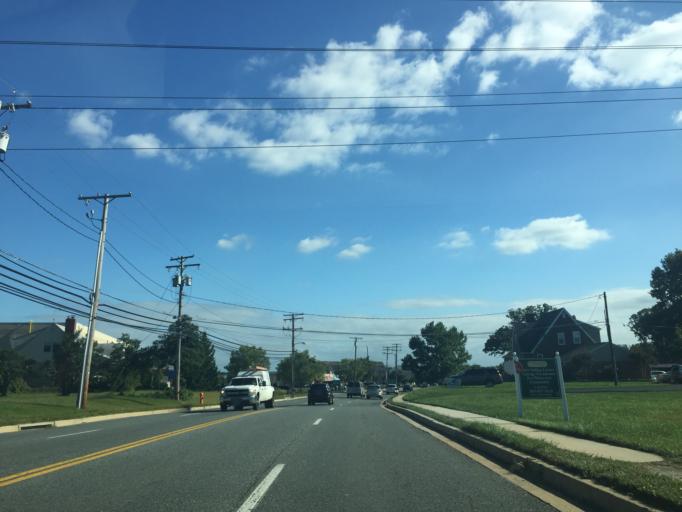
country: US
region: Maryland
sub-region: Baltimore County
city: Middle River
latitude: 39.3507
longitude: -76.4517
